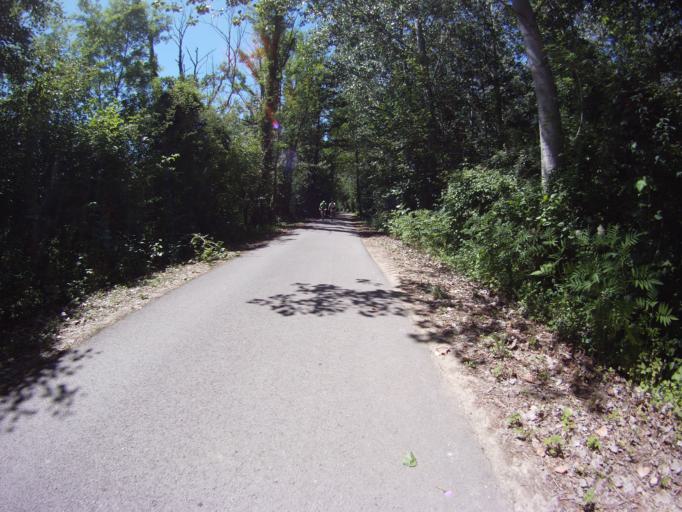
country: FR
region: Champagne-Ardenne
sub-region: Departement de la Marne
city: Damery
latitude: 49.0654
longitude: 3.8947
